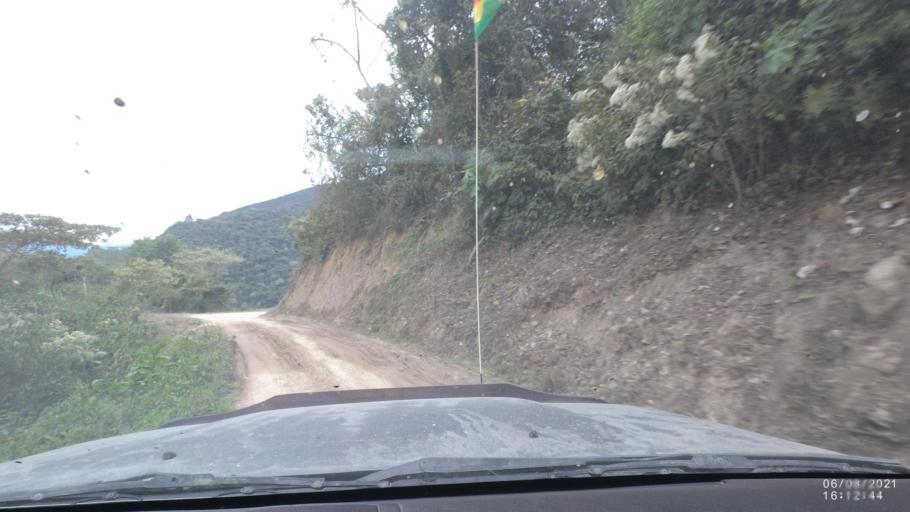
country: BO
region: La Paz
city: Quime
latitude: -16.5564
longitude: -66.7379
